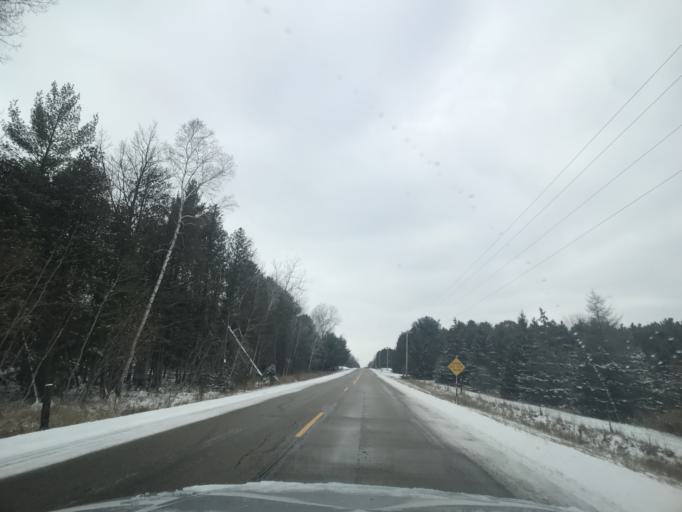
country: US
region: Wisconsin
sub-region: Brown County
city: Suamico
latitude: 44.7062
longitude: -88.0892
